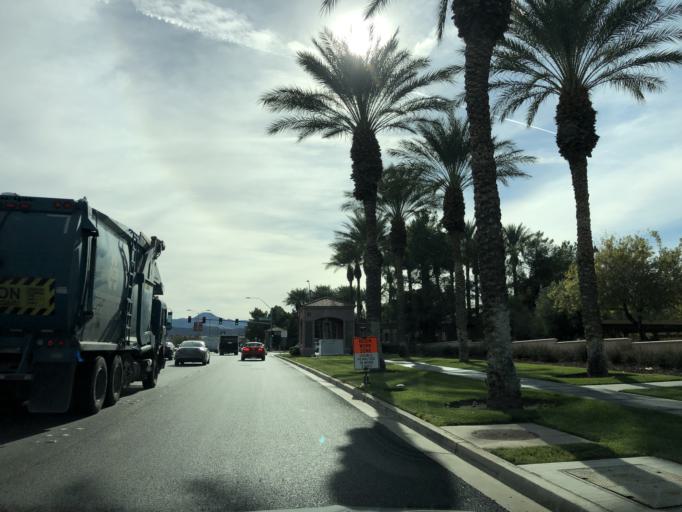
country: US
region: Nevada
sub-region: Clark County
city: Whitney
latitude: 36.0215
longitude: -115.0840
